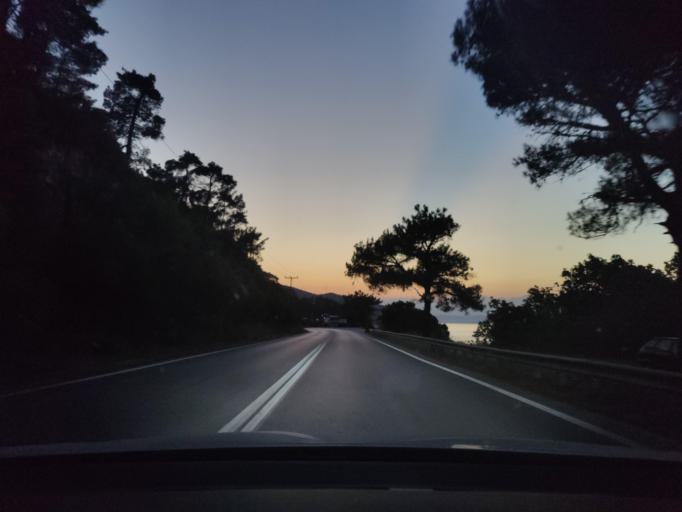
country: GR
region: East Macedonia and Thrace
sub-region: Nomos Kavalas
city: Thasos
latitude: 40.7781
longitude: 24.6901
